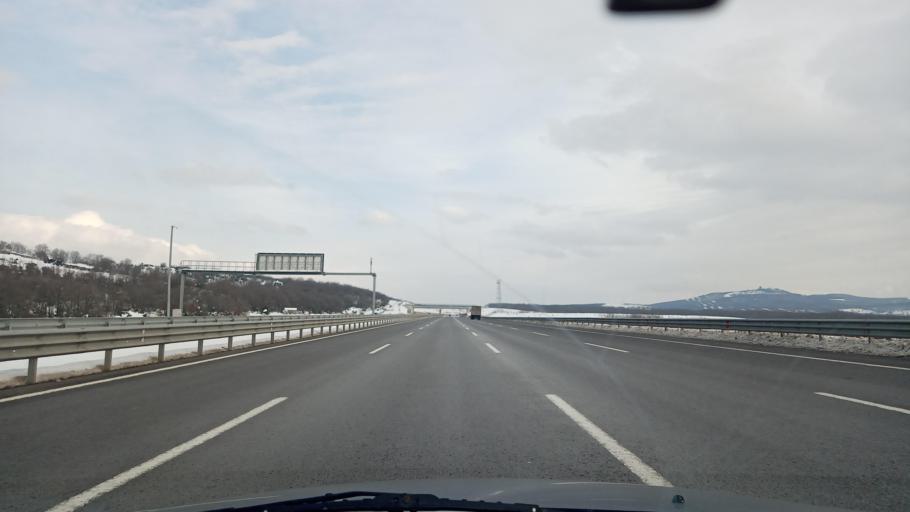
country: TR
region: Kocaeli
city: Mollafeneri
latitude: 40.8891
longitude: 29.5878
